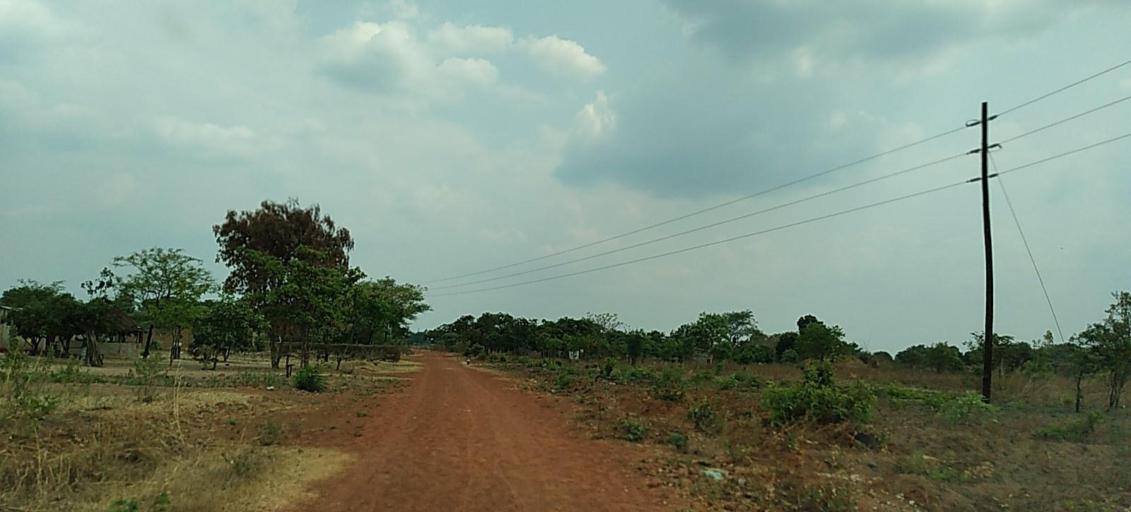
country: ZM
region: Copperbelt
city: Kalulushi
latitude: -12.8894
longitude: 28.0749
